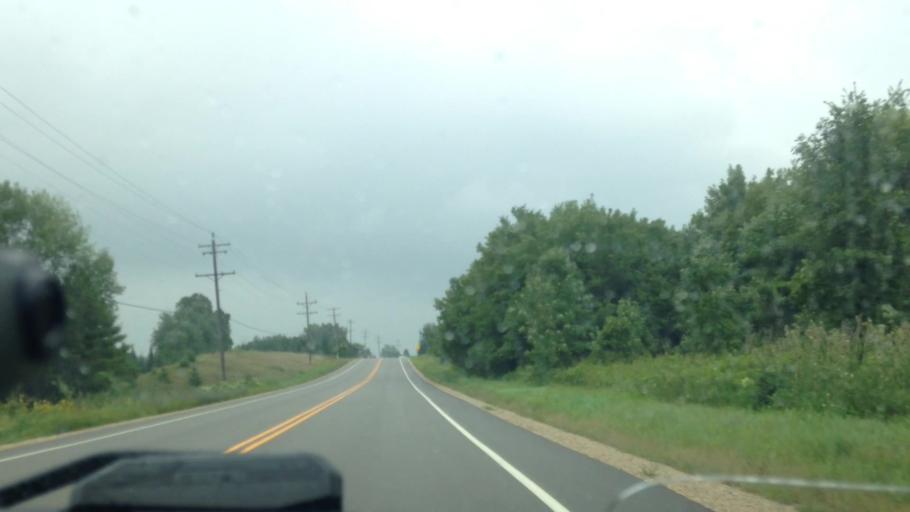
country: US
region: Wisconsin
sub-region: Washington County
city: Richfield
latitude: 43.2991
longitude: -88.2257
